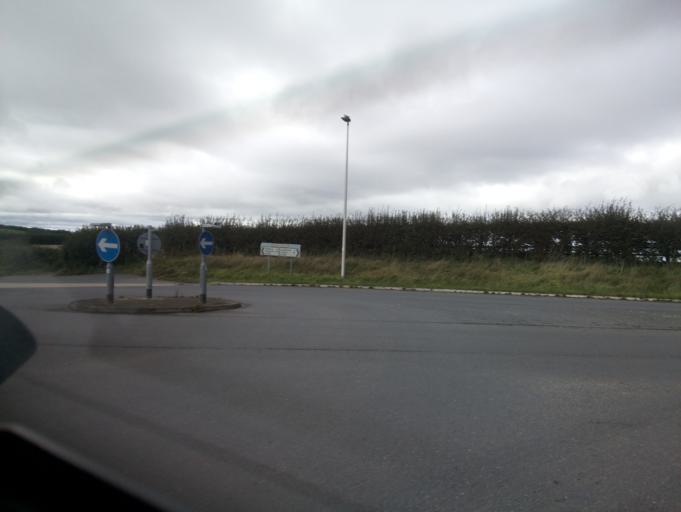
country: GB
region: England
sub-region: Devon
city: Kingsbridge
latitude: 50.2974
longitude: -3.7978
